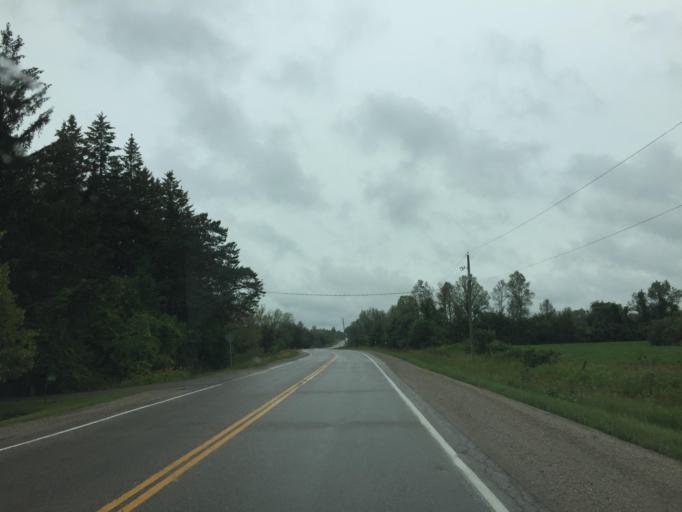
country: CA
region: Ontario
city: Cambridge
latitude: 43.4329
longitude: -80.2613
